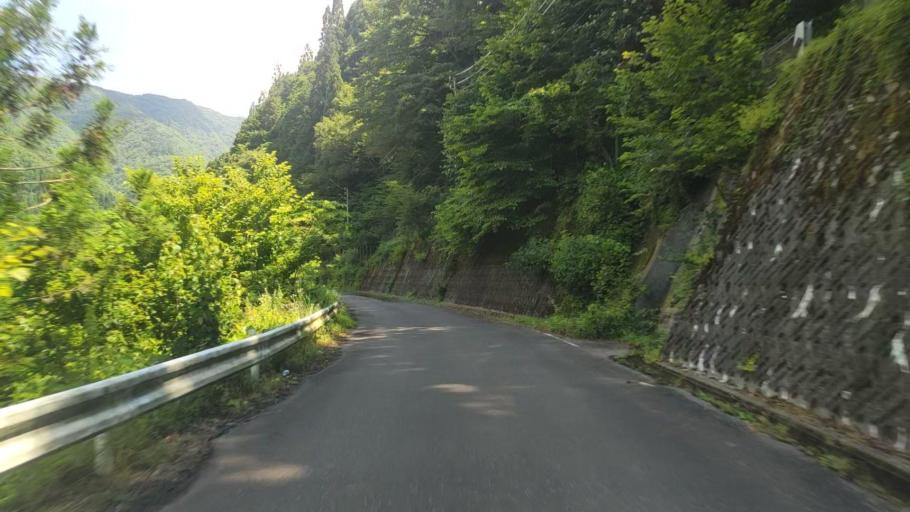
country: JP
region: Gifu
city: Godo
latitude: 35.7041
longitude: 136.5876
